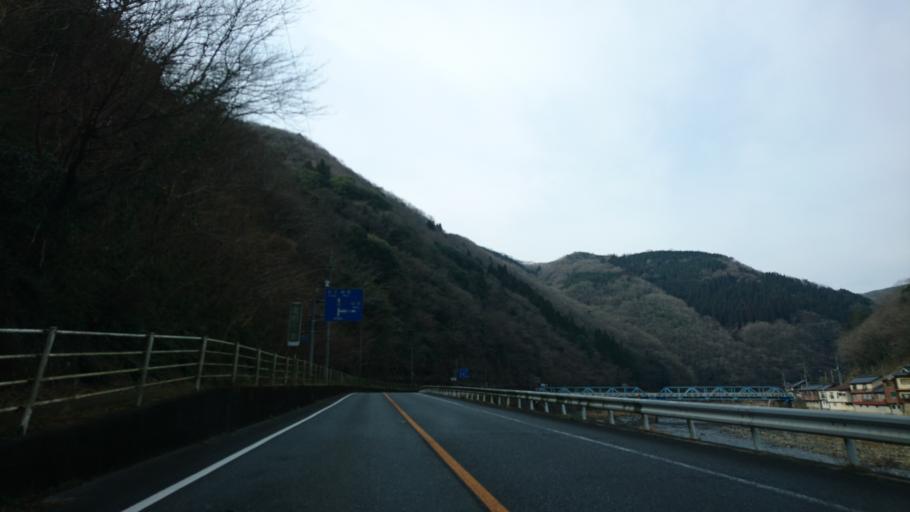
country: JP
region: Okayama
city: Takahashi
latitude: 34.8758
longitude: 133.5582
